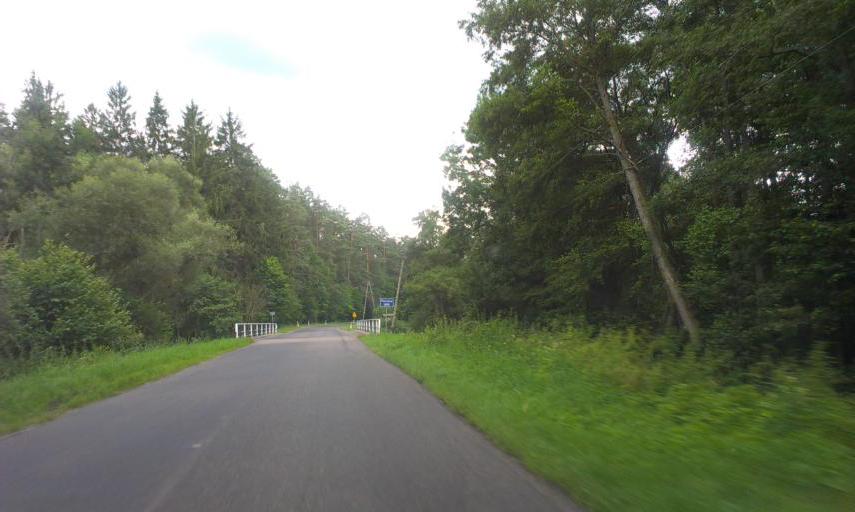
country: PL
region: West Pomeranian Voivodeship
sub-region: Powiat bialogardzki
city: Tychowo
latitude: 53.8735
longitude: 16.1768
